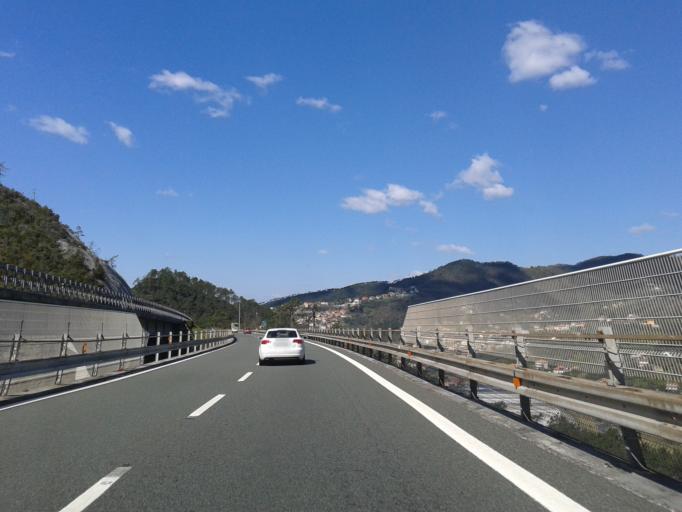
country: IT
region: Liguria
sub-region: Provincia di Genova
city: Casarza Ligure
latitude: 44.2710
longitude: 9.4711
